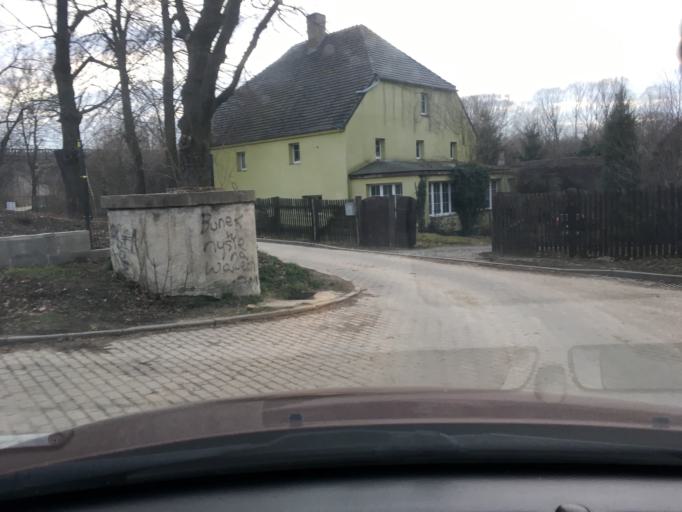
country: PL
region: Lower Silesian Voivodeship
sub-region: Powiat zgorzelecki
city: Zgorzelec
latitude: 51.1422
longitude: 14.9971
